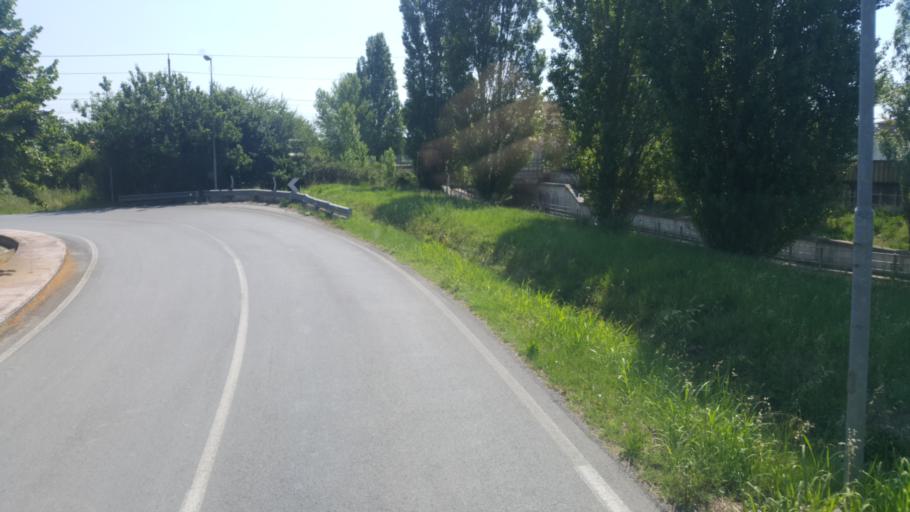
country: IT
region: Umbria
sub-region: Provincia di Perugia
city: Castiglione del Lago
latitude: 43.1246
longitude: 12.0304
